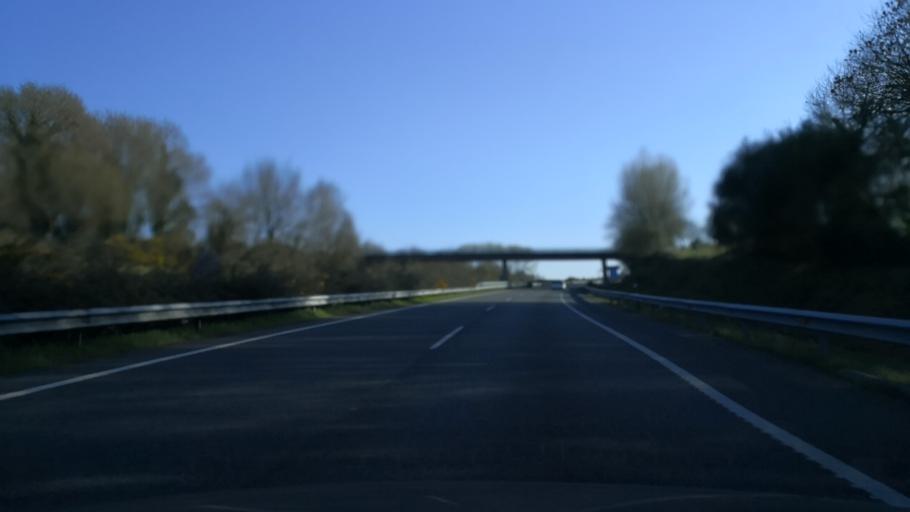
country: ES
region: Galicia
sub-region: Provincia de Lugo
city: Lugo
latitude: 42.9830
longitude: -7.5013
